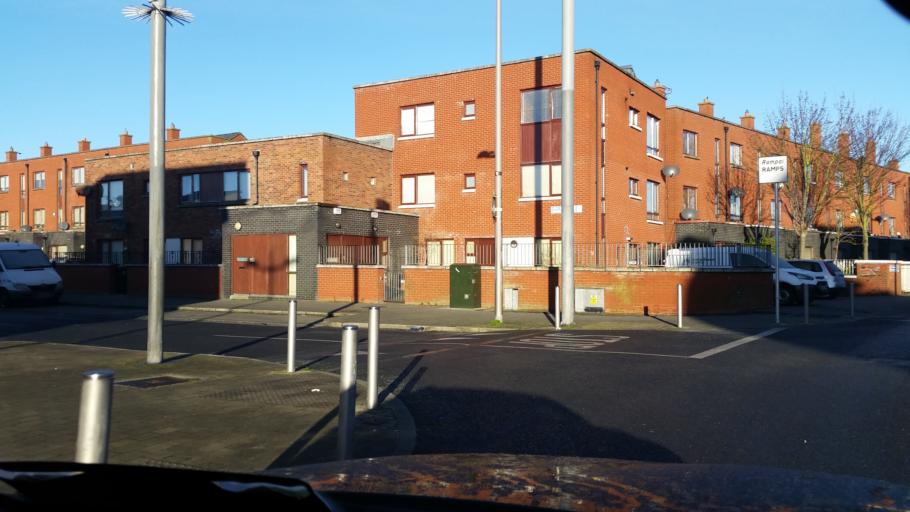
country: IE
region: Leinster
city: Ballymun
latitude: 53.3968
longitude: -6.2753
